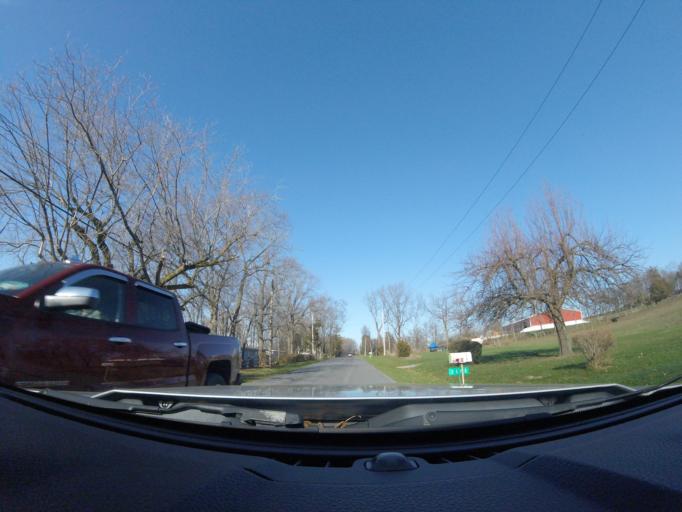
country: US
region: New York
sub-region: Cayuga County
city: Union Springs
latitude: 42.7245
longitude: -76.7092
